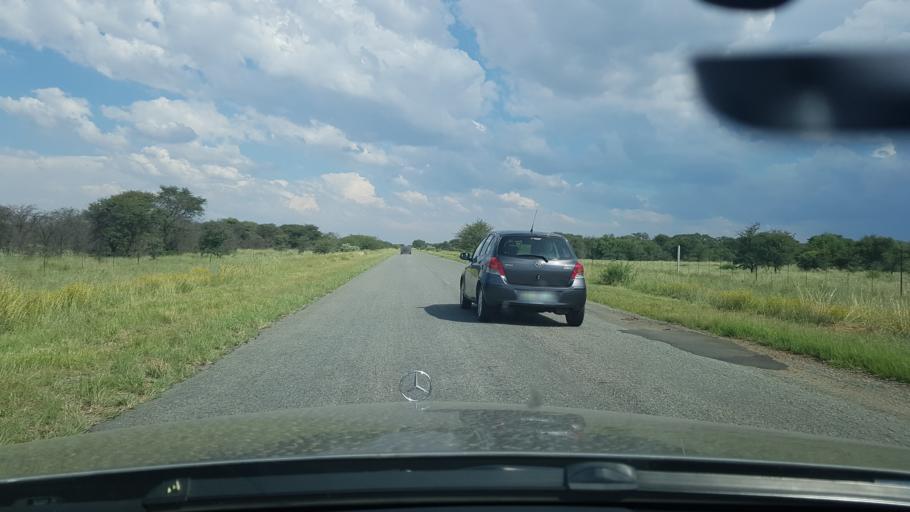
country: ZA
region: North-West
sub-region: Dr Ruth Segomotsi Mompati District Municipality
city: Bloemhof
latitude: -27.7799
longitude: 25.6085
